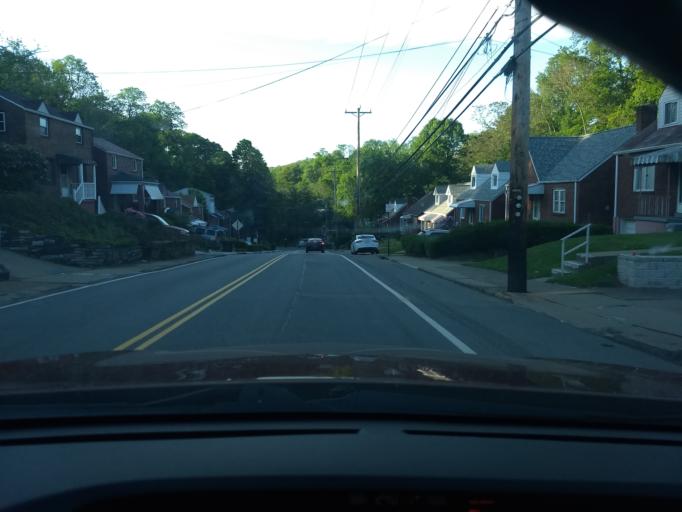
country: US
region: Pennsylvania
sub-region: Allegheny County
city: White Oak
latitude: 40.3512
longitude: -79.8342
